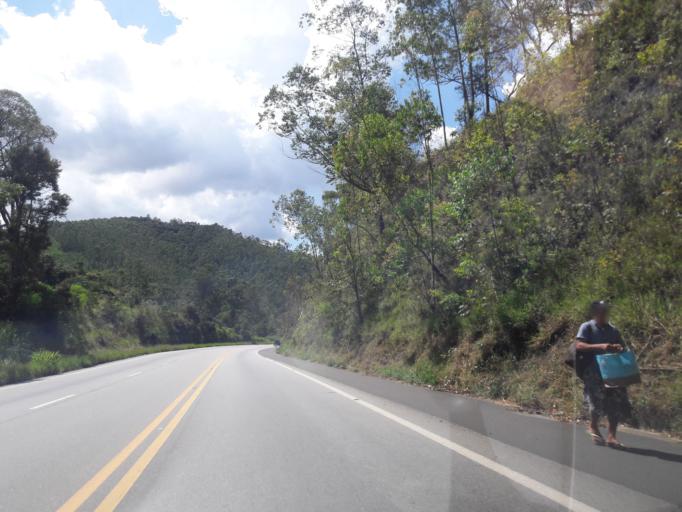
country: BR
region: Sao Paulo
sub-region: Campo Limpo Paulista
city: Campo Limpo Paulista
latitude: -23.2570
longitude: -46.7912
